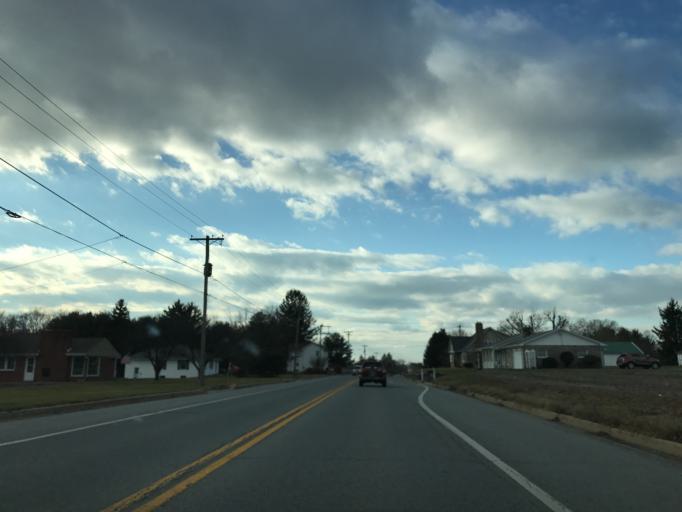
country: US
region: Maryland
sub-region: Cecil County
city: Rising Sun
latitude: 39.6906
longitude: -76.0467
